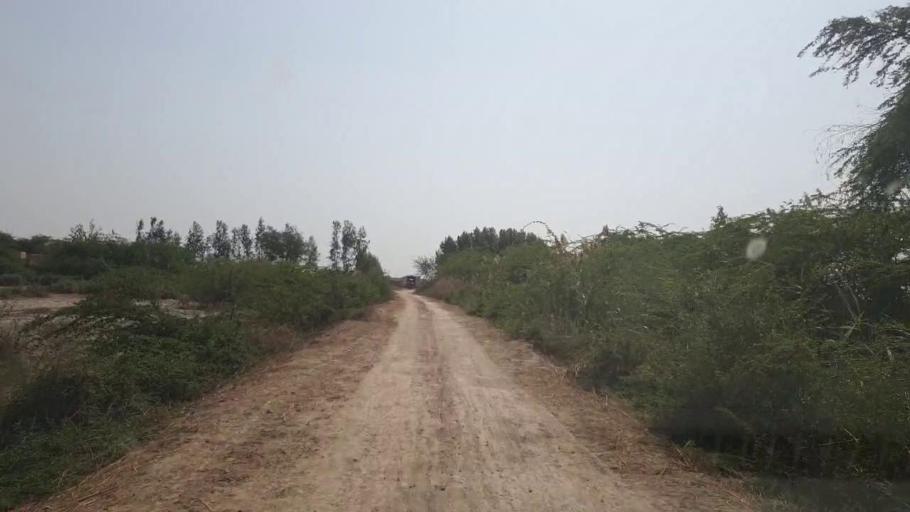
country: PK
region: Sindh
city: Jati
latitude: 24.4668
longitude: 68.5546
